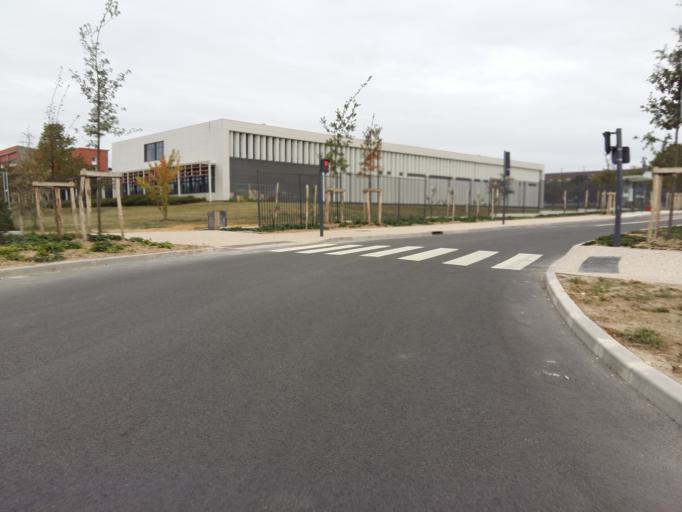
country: FR
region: Picardie
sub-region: Departement de la Somme
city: Amiens
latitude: 49.8751
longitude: 2.3008
